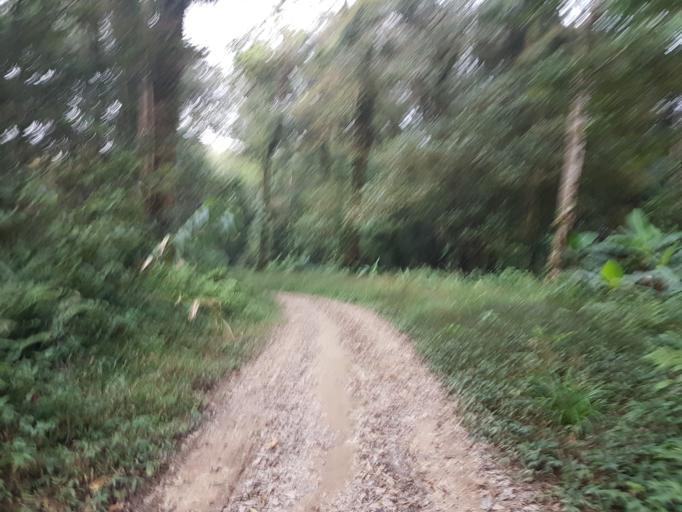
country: TH
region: Phetchabun
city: Lom Kao
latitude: 16.8923
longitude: 101.0940
